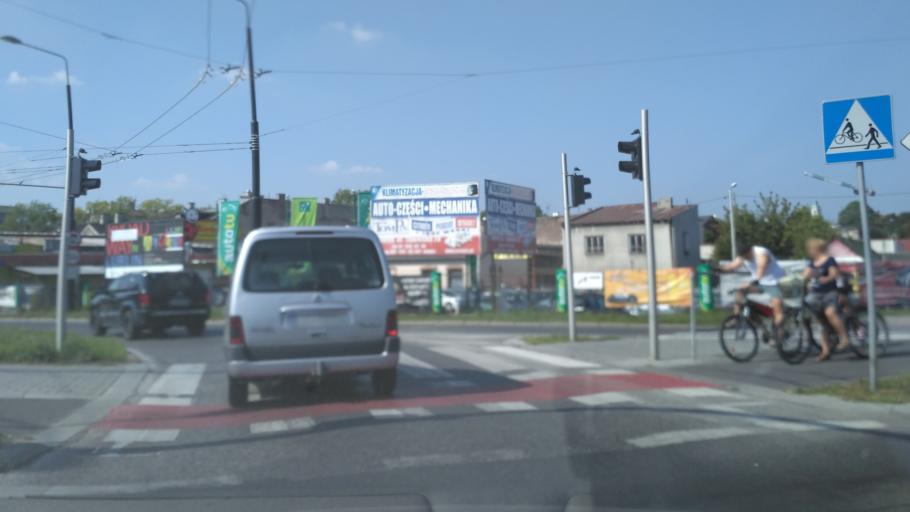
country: PL
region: Lublin Voivodeship
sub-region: Powiat lubelski
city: Lublin
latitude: 51.2403
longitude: 22.5723
